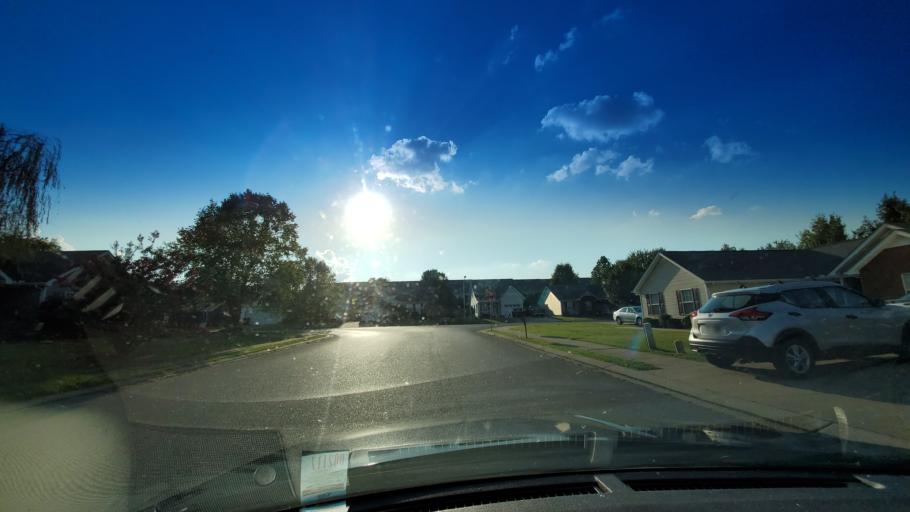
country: US
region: Tennessee
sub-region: Rutherford County
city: Murfreesboro
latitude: 35.7817
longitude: -86.4037
